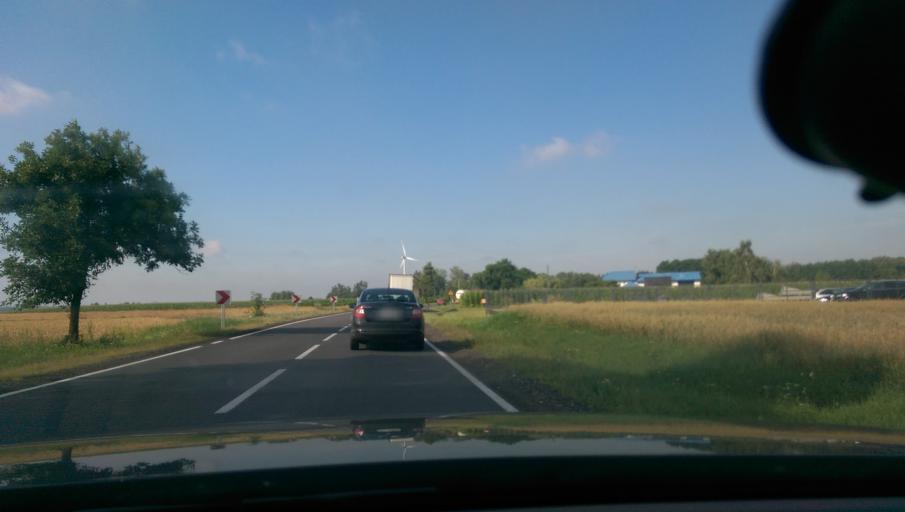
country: PL
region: Masovian Voivodeship
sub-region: Powiat plonski
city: Plonsk
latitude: 52.6478
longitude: 20.4238
